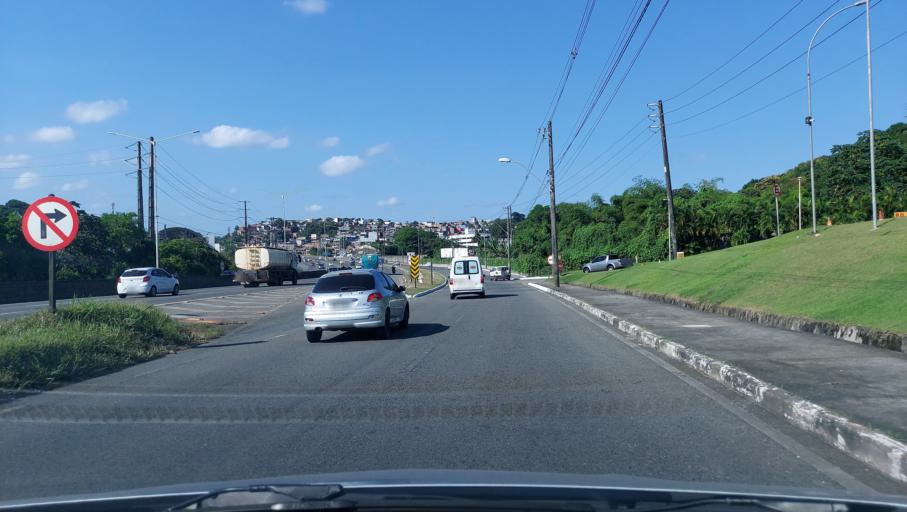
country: BR
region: Bahia
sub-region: Salvador
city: Salvador
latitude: -12.9593
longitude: -38.4728
